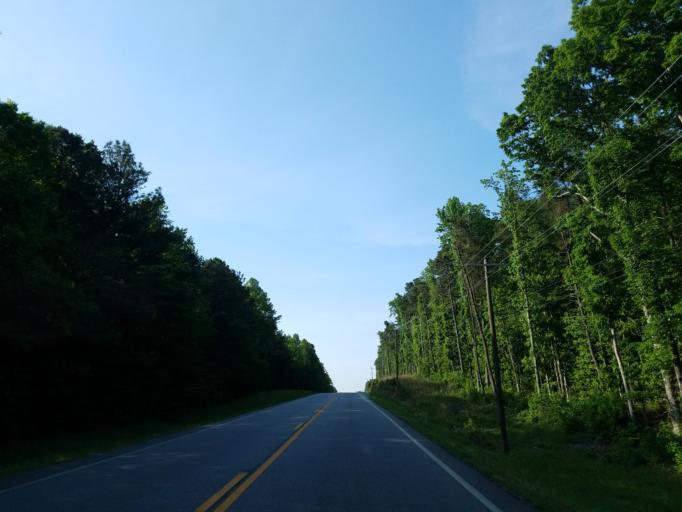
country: US
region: Georgia
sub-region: Whitfield County
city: Dalton
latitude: 34.6599
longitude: -85.0594
